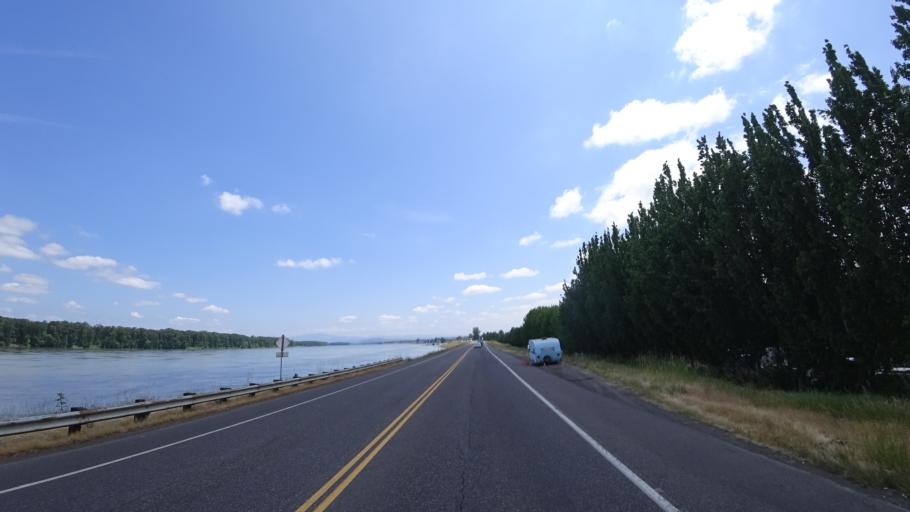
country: US
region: Washington
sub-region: Clark County
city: Mill Plain
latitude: 45.5724
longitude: -122.5442
